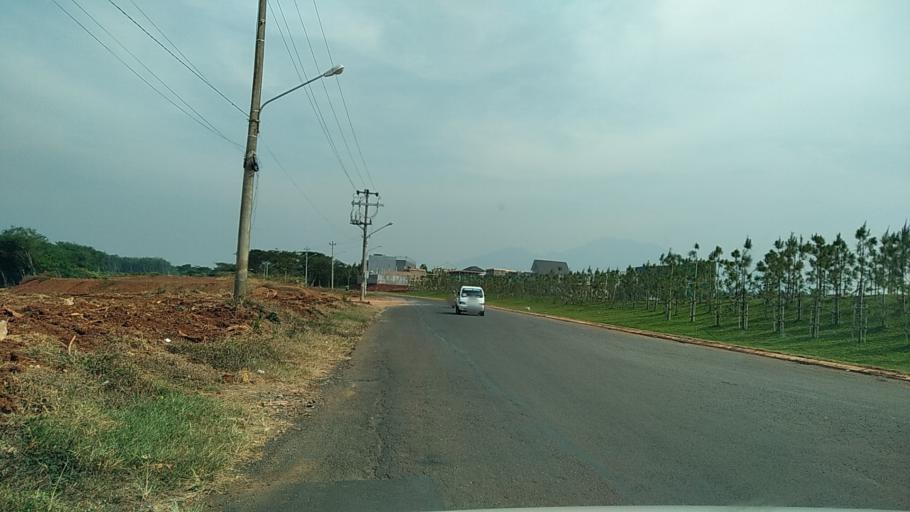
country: ID
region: Central Java
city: Semarang
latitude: -7.0392
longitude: 110.3178
